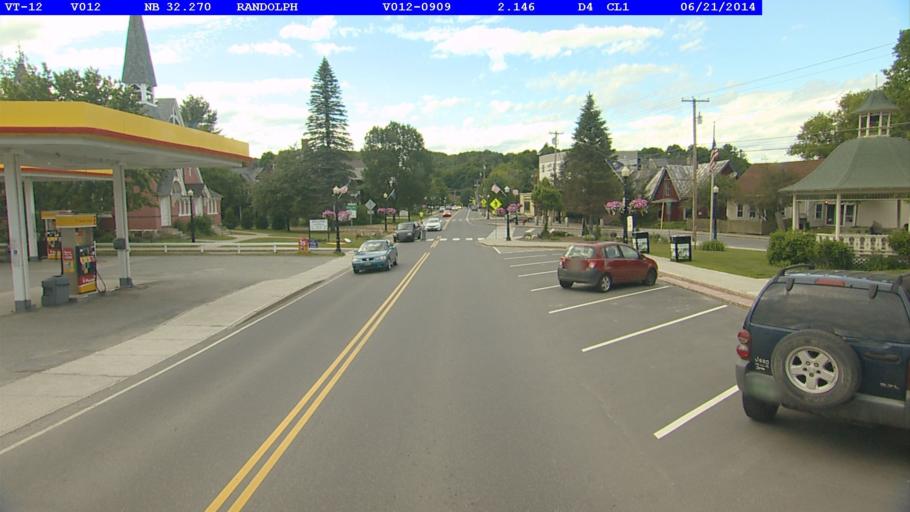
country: US
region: Vermont
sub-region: Orange County
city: Randolph
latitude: 43.9235
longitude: -72.6651
